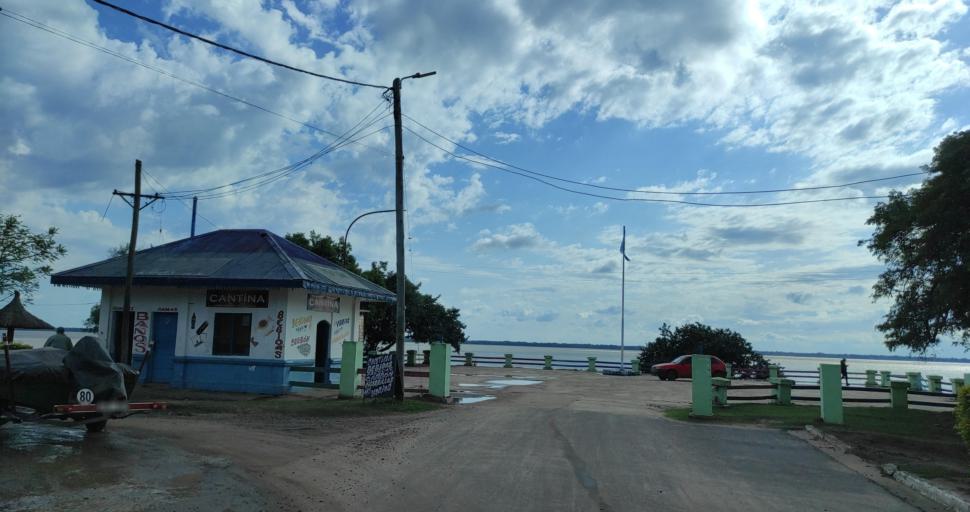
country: AR
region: Corrientes
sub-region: Departamento de Itati
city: Itati
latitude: -27.2670
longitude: -58.2477
